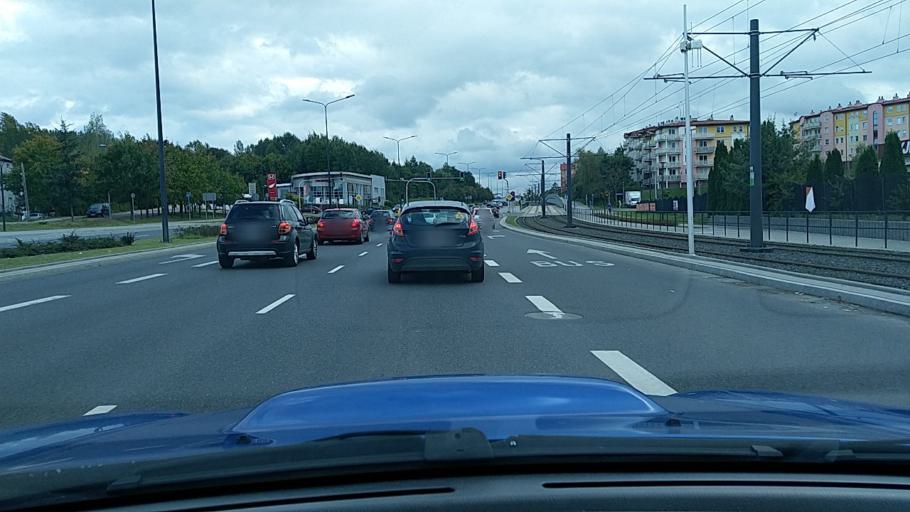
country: PL
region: Warmian-Masurian Voivodeship
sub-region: Olsztyn
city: Kortowo
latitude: 53.7482
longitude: 20.4869
